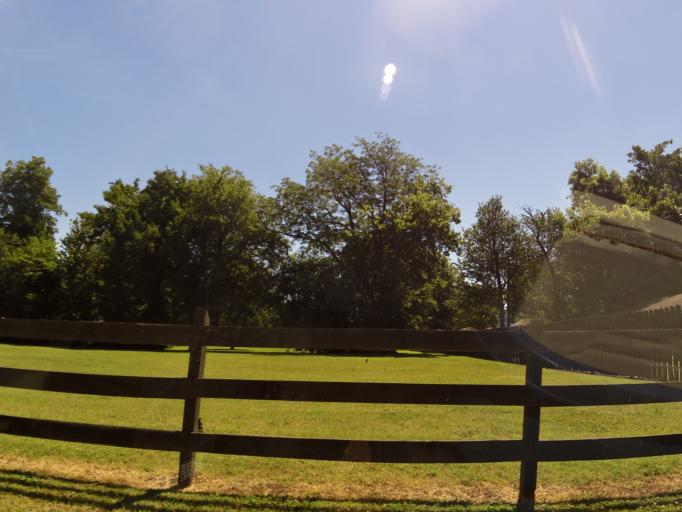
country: US
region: Missouri
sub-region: New Madrid County
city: New Madrid
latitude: 36.5849
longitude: -89.5340
